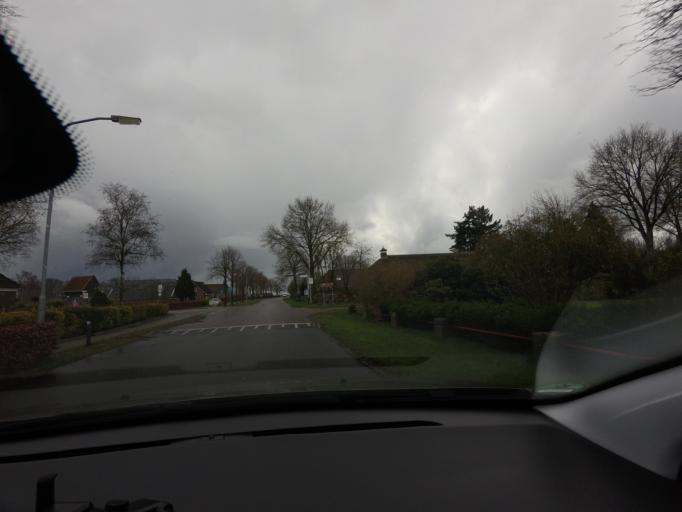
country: NL
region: Drenthe
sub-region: Gemeente Borger-Odoorn
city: Borger
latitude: 52.9520
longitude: 6.7904
